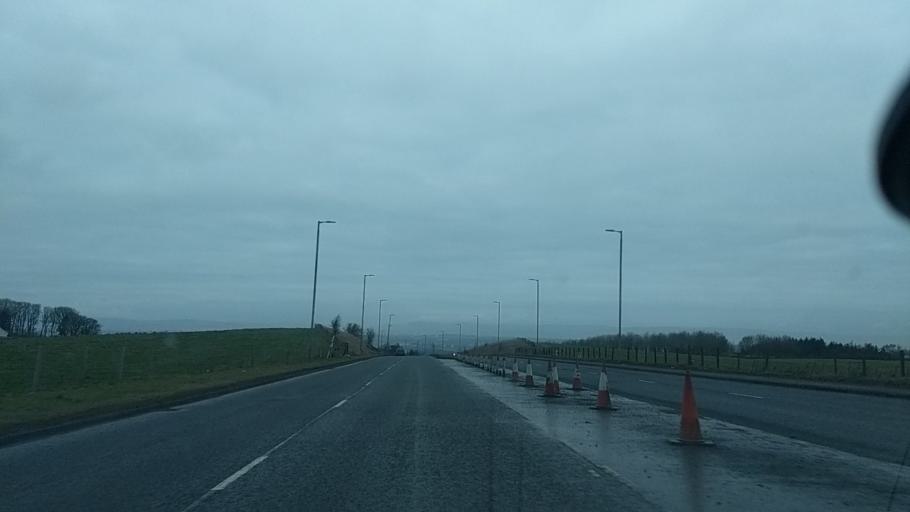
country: GB
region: Scotland
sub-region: South Lanarkshire
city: East Kilbride
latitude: 55.7944
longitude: -4.1677
